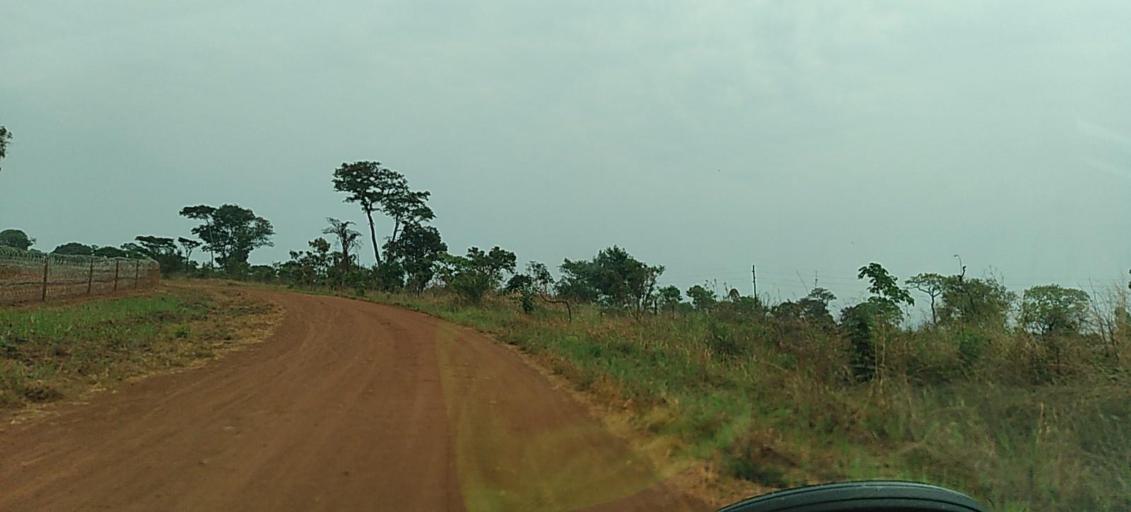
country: ZM
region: North-Western
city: Kansanshi
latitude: -12.0939
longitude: 26.4924
